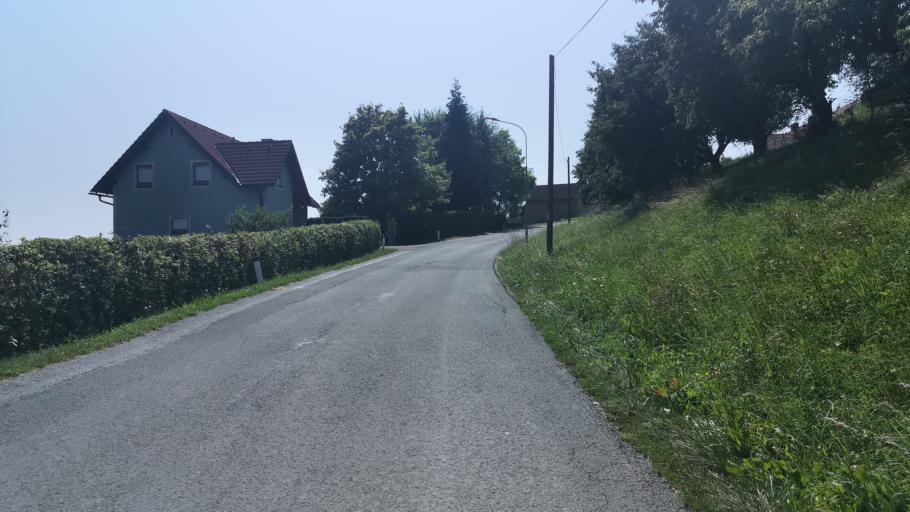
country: AT
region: Styria
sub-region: Politischer Bezirk Deutschlandsberg
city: Lannach
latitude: 46.9340
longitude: 15.3505
